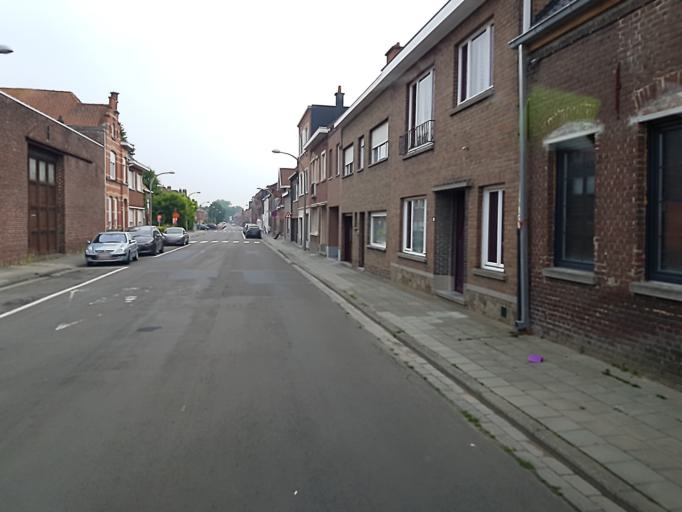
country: BE
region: Flanders
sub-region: Provincie West-Vlaanderen
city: Kortrijk
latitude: 50.8217
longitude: 3.2285
